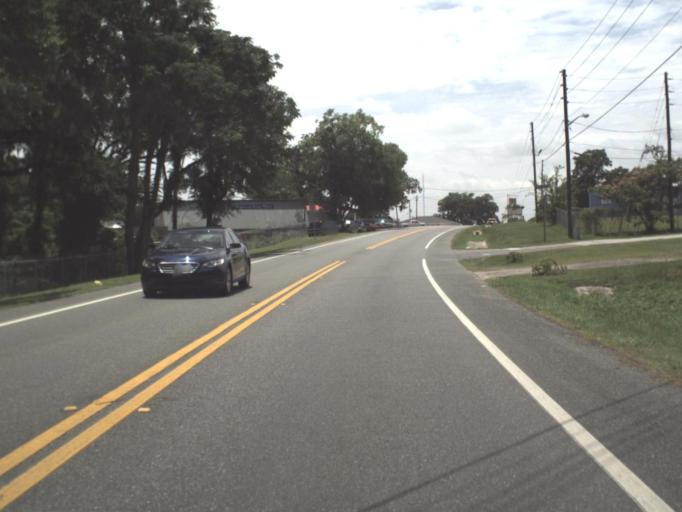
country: US
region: Florida
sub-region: Madison County
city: Madison
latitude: 30.4505
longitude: -83.4193
